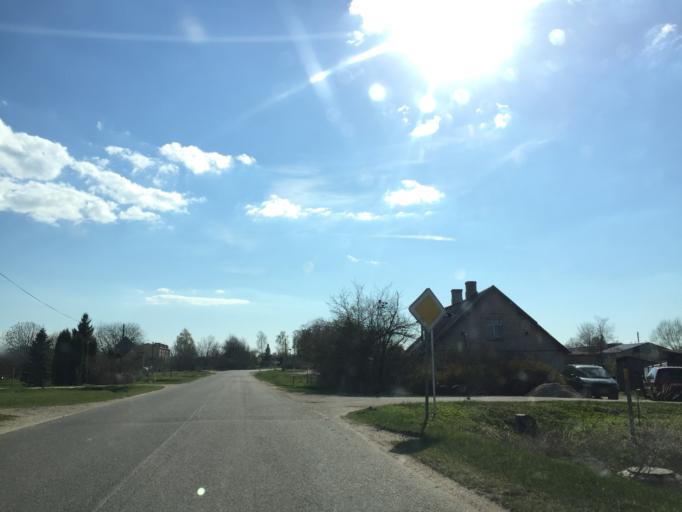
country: LV
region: Saulkrastu
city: Saulkrasti
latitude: 57.3316
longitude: 24.4948
